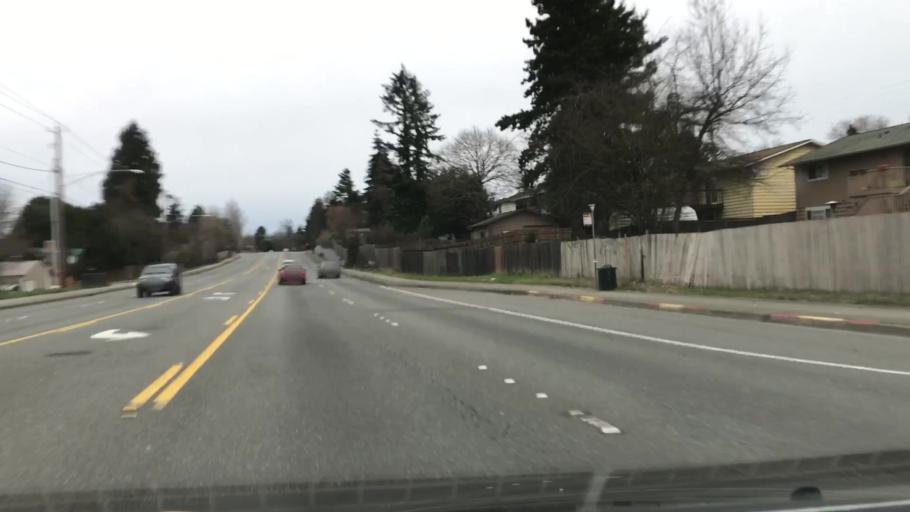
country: US
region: Washington
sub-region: King County
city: East Hill-Meridian
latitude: 47.3948
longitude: -122.2024
